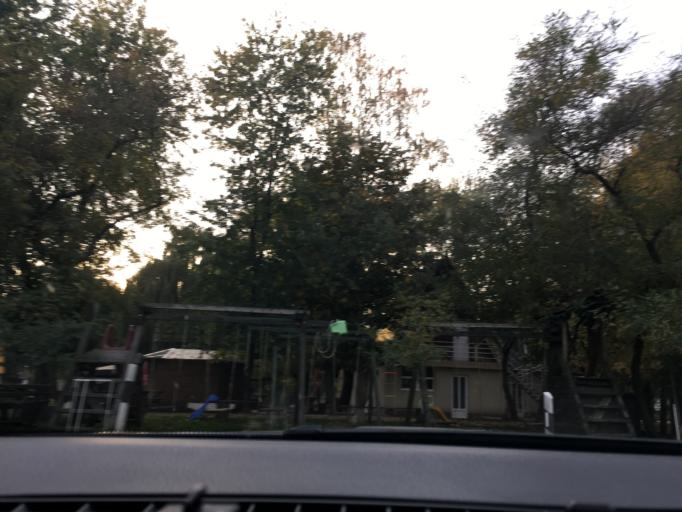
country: HU
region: Szabolcs-Szatmar-Bereg
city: Mariapocs
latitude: 47.8641
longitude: 22.0287
